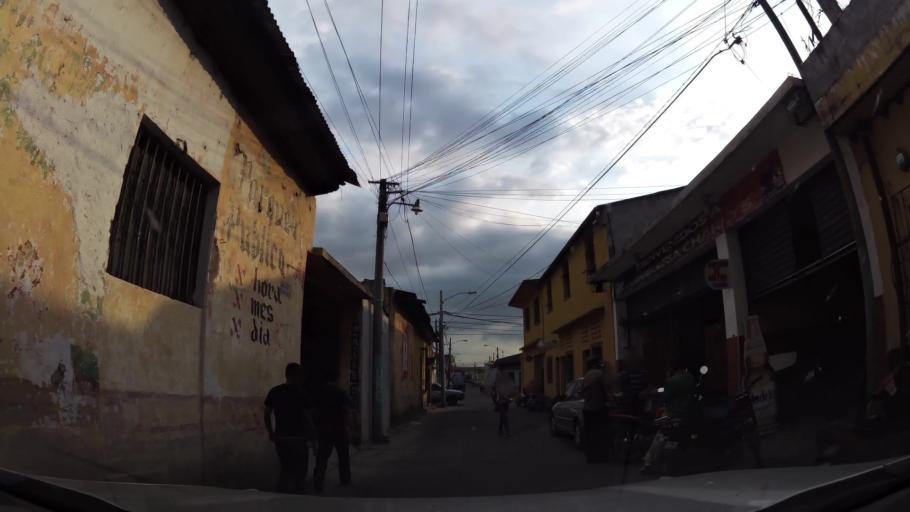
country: GT
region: Escuintla
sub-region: Municipio de Escuintla
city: Escuintla
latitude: 14.3041
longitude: -90.7852
